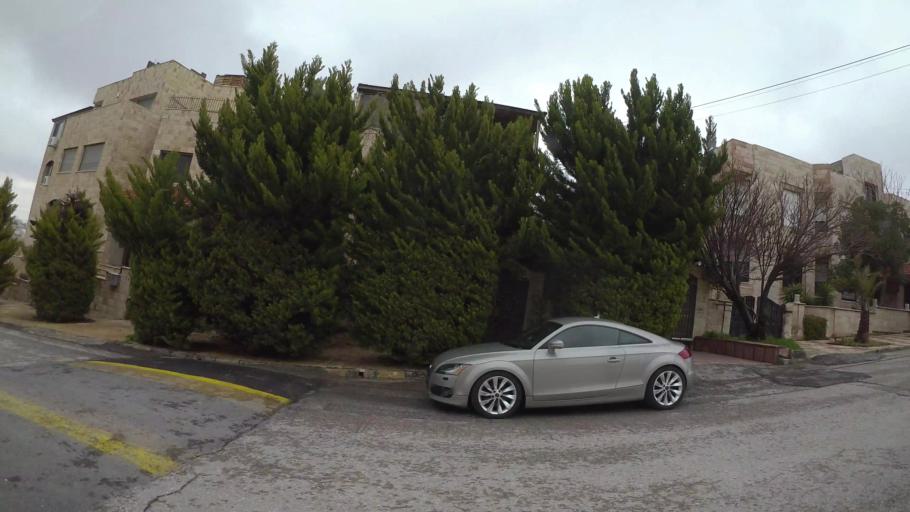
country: JO
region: Amman
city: Al Bunayyat ash Shamaliyah
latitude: 31.9436
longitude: 35.8848
